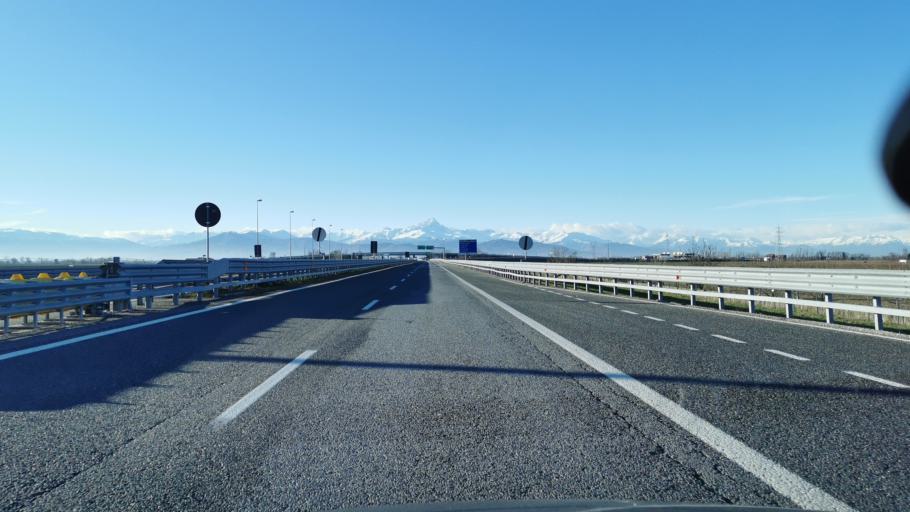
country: IT
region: Piedmont
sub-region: Provincia di Cuneo
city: Montanera
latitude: 44.4743
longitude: 7.6991
